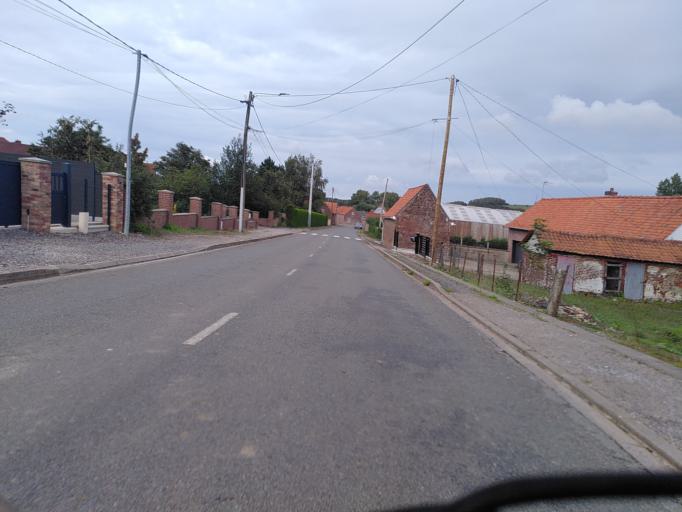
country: FR
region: Nord-Pas-de-Calais
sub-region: Departement du Pas-de-Calais
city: Therouanne
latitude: 50.6021
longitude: 2.1770
